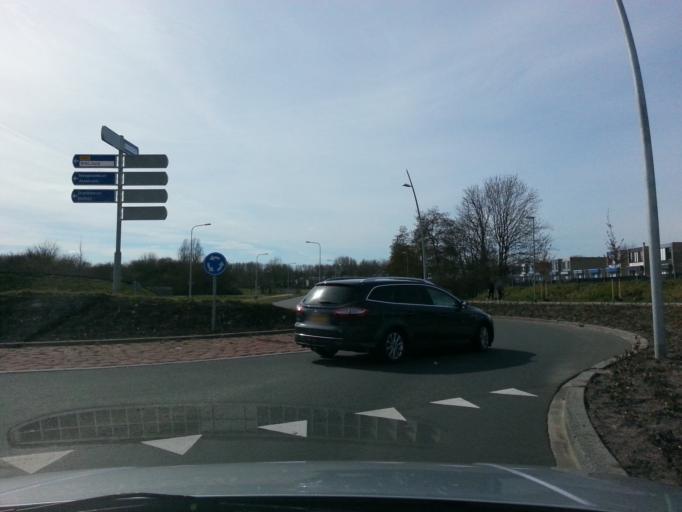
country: NL
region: Groningen
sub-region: Gemeente Groningen
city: Oosterpark
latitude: 53.2414
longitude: 6.5849
